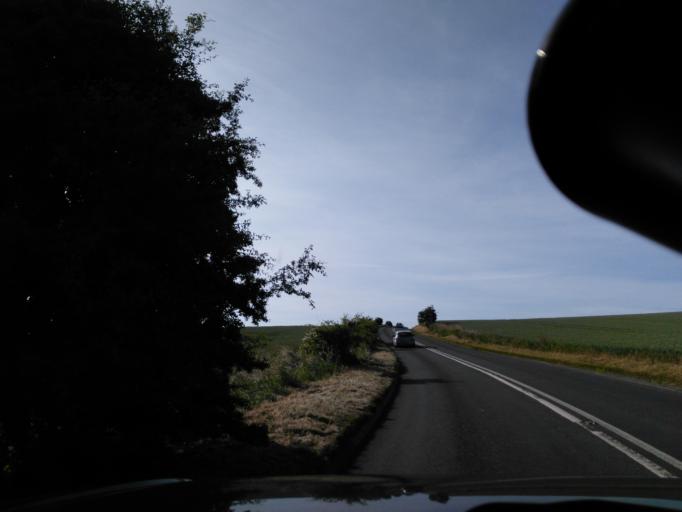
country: GB
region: England
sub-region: Wiltshire
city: Woodford
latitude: 51.1211
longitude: -1.8543
